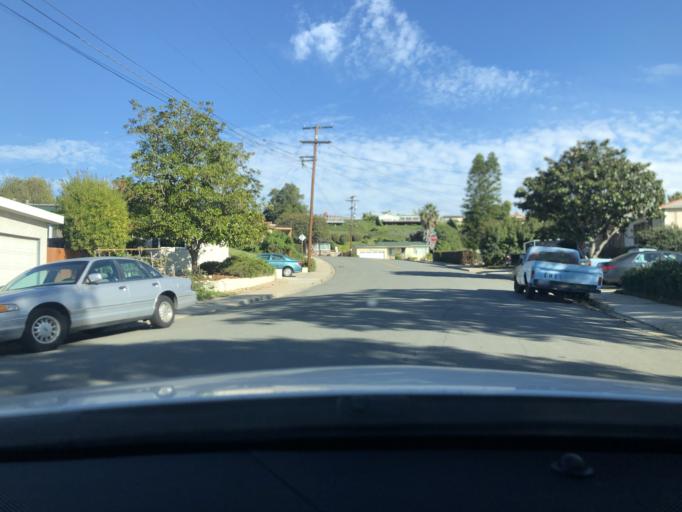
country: US
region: California
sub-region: San Diego County
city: Lemon Grove
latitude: 32.7529
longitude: -117.0728
